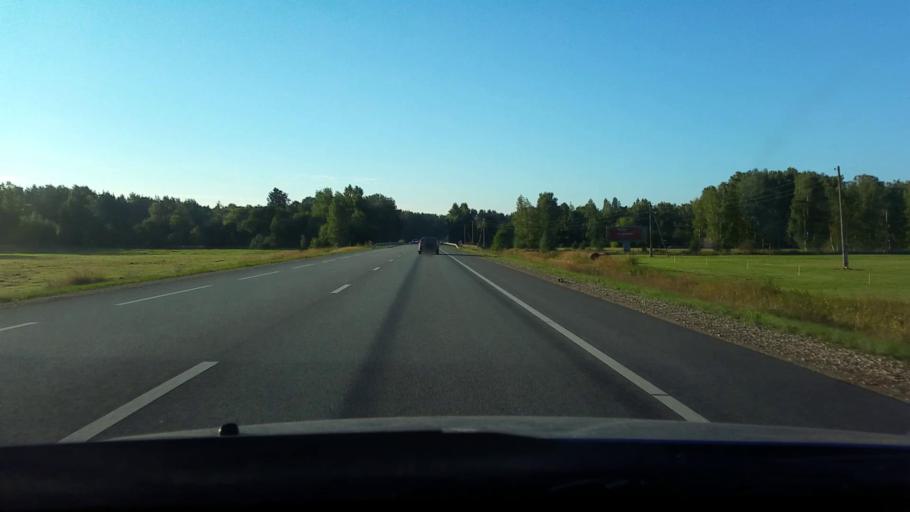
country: LV
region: Adazi
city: Adazi
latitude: 57.0663
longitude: 24.3206
